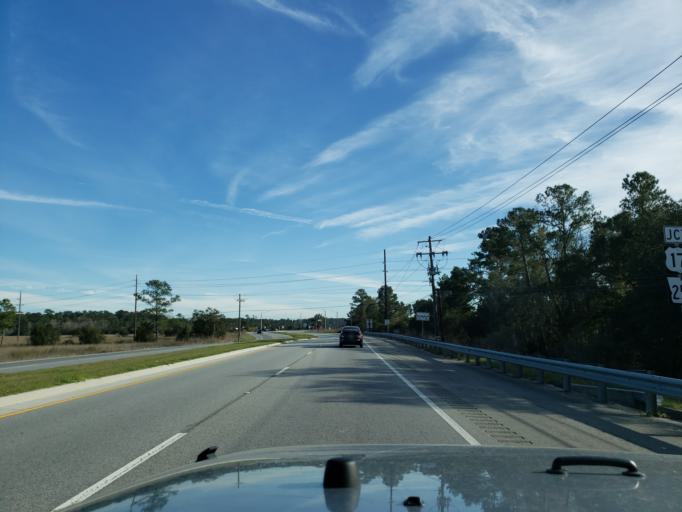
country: US
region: Georgia
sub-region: Chatham County
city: Georgetown
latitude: 32.0417
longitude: -81.2102
